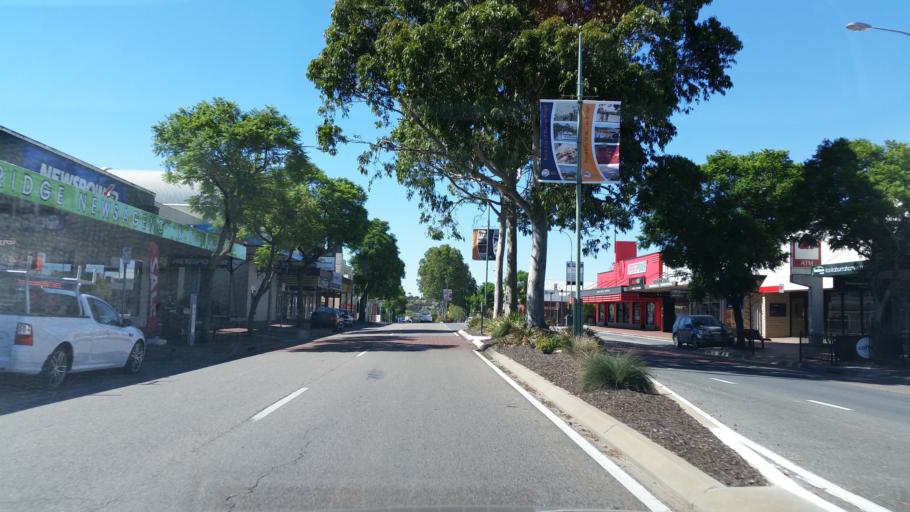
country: AU
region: South Australia
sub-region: Murray Bridge
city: Murray Bridge
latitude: -35.1189
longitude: 139.2757
